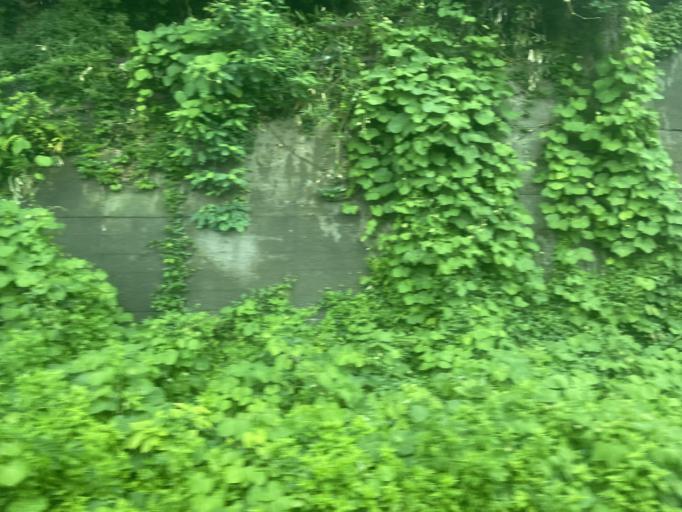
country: JP
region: Niigata
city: Kashiwazaki
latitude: 37.3615
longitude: 138.5473
